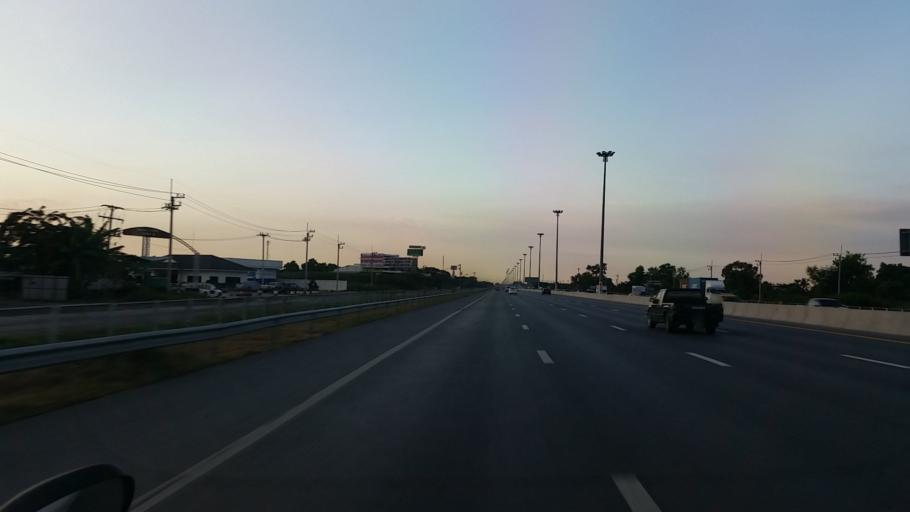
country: TH
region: Pathum Thani
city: Khlong Luang
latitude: 14.0894
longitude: 100.6929
